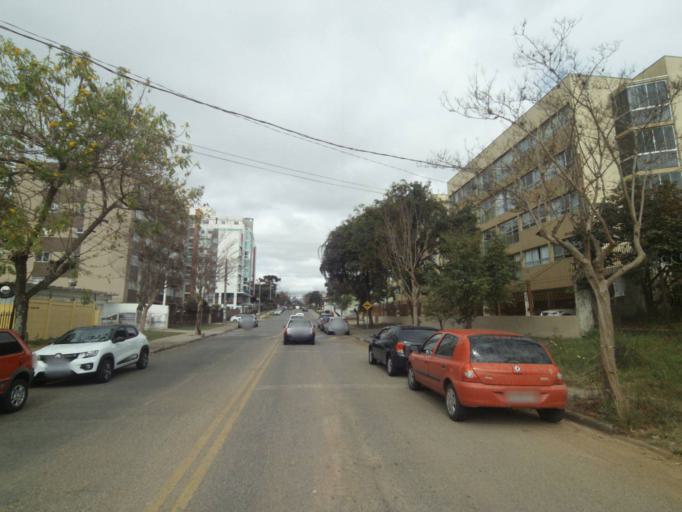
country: BR
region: Parana
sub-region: Curitiba
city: Curitiba
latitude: -25.4622
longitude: -49.2873
